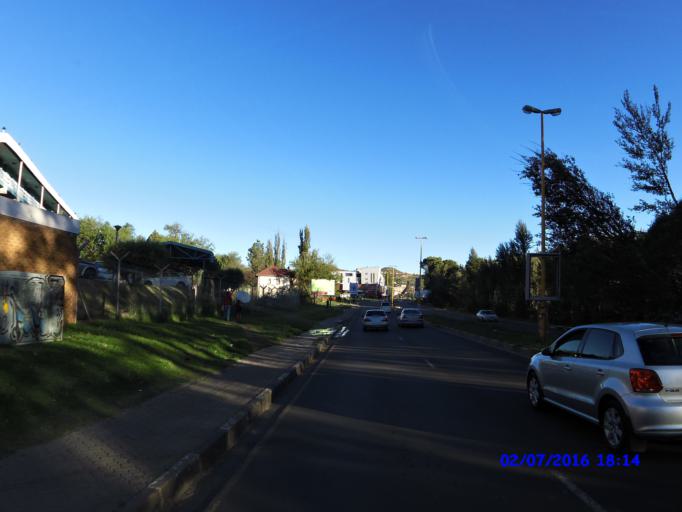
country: LS
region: Maseru
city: Maseru
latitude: -29.3092
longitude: 27.4741
